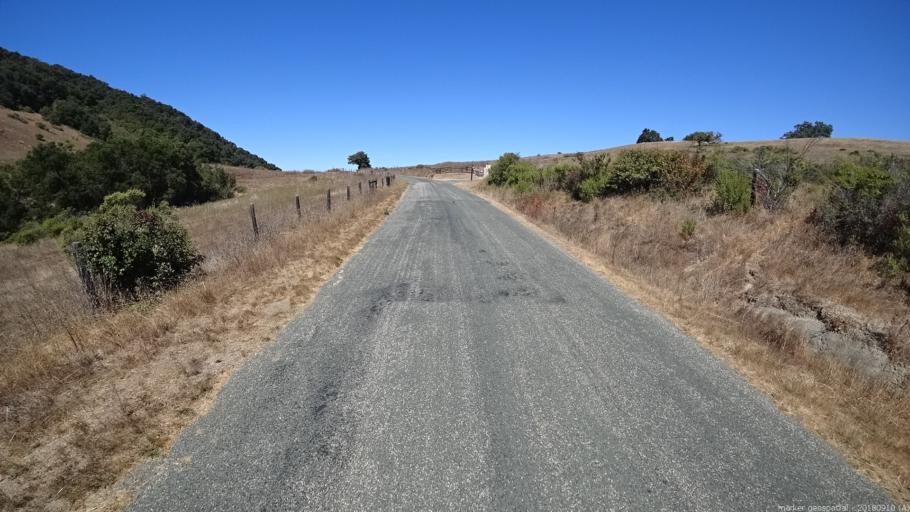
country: US
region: California
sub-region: Monterey County
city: Carmel Valley Village
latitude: 36.4697
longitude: -121.8014
